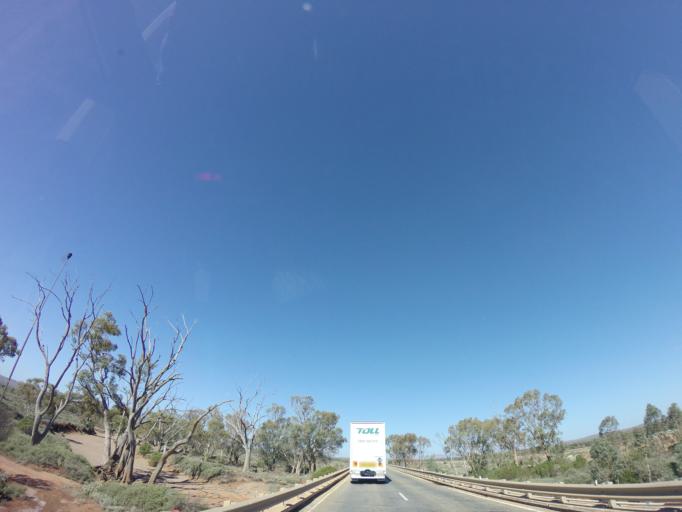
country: AU
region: South Australia
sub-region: Peterborough
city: Peterborough
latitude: -32.5771
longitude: 139.5725
